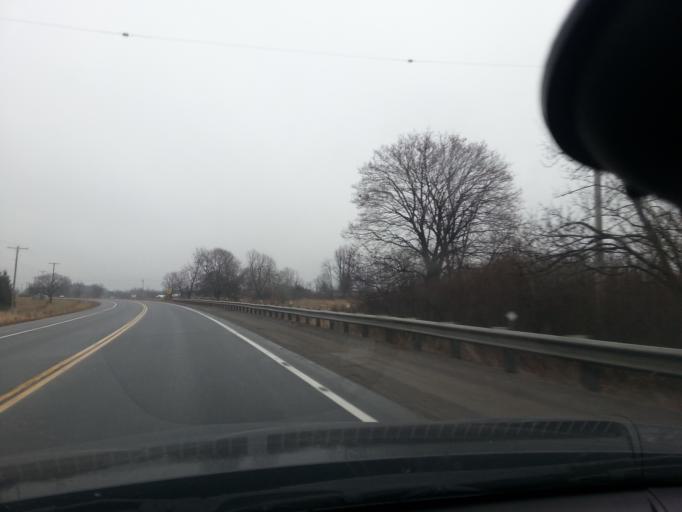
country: CA
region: Ontario
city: Quinte West
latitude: 44.5130
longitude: -77.4669
